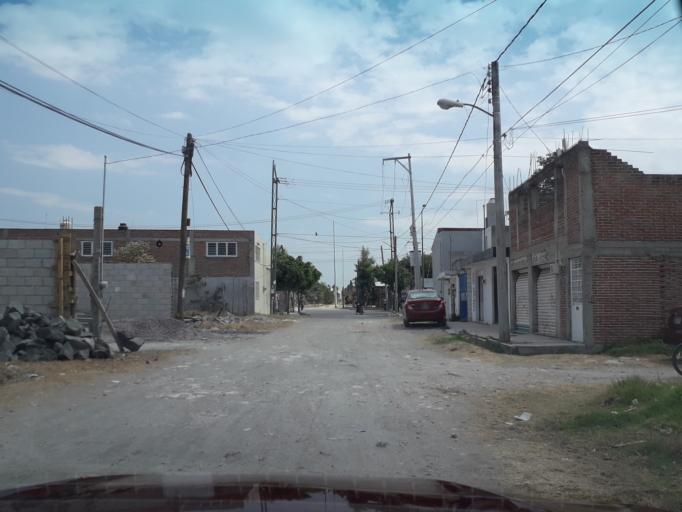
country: MX
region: Puebla
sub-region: Puebla
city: El Capulo (La Quebradora)
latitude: 18.9680
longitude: -98.2600
